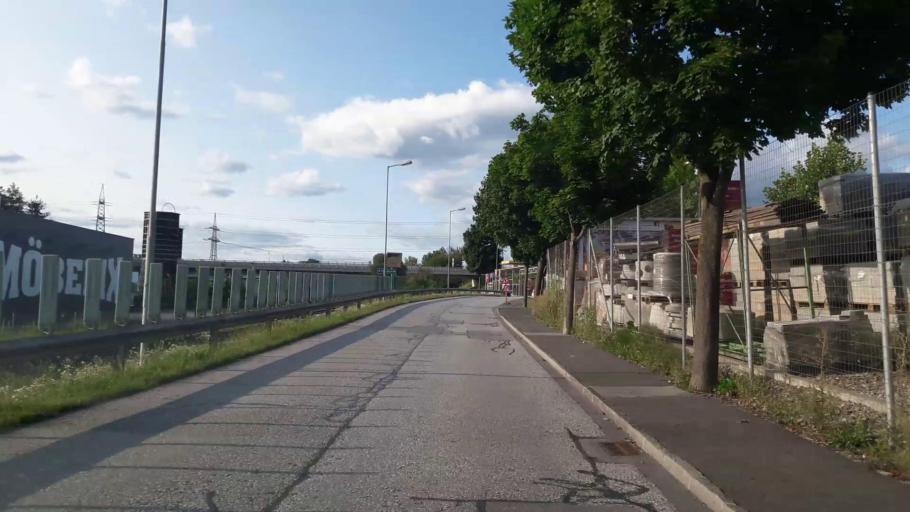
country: AT
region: Styria
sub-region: Politischer Bezirk Weiz
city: Gleisdorf
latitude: 47.1098
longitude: 15.7042
